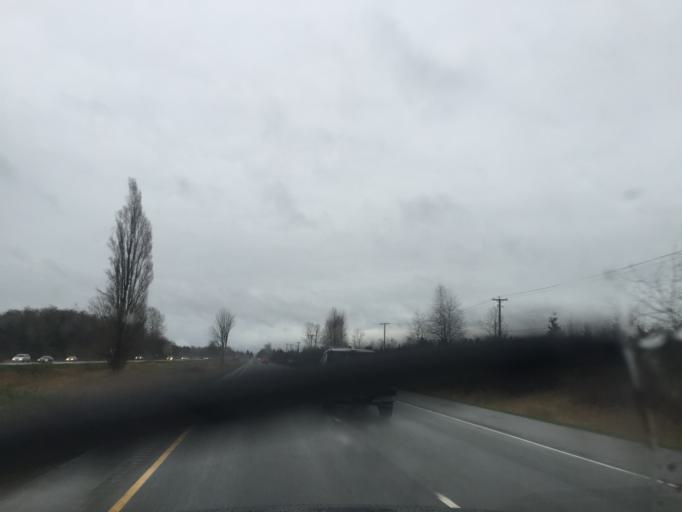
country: CA
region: British Columbia
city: Aldergrove
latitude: 49.0887
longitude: -122.4605
